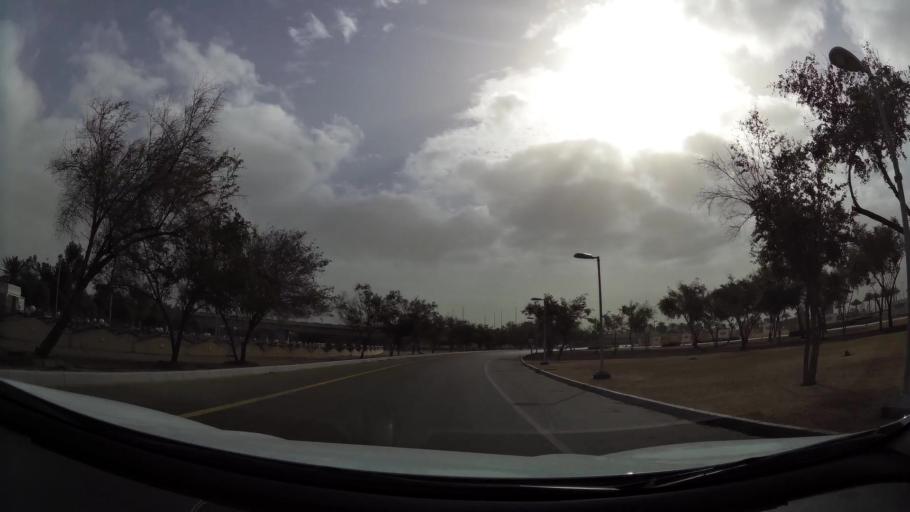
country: AE
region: Abu Dhabi
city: Abu Dhabi
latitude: 24.4180
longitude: 54.4758
